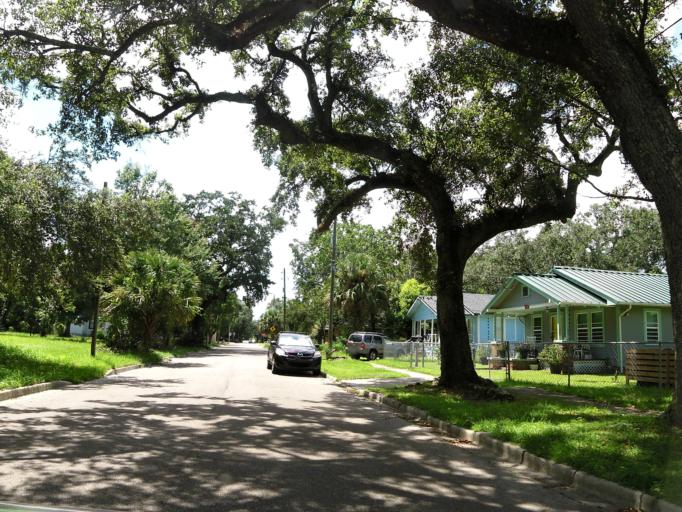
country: US
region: Florida
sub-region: Duval County
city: Jacksonville
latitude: 30.3507
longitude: -81.6397
